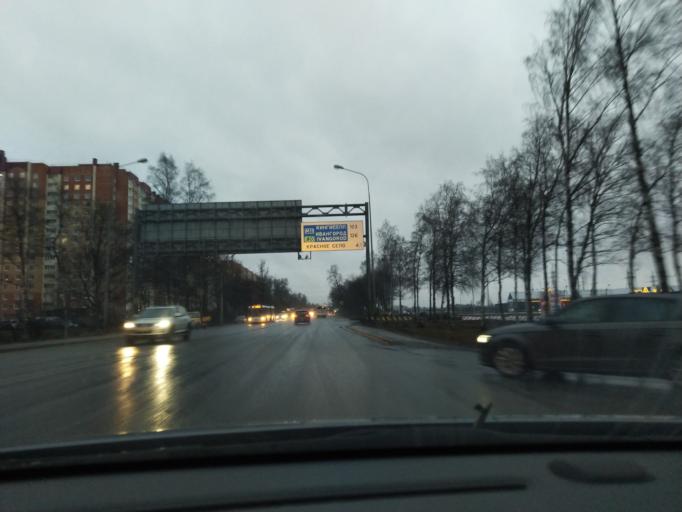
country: RU
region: St.-Petersburg
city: Gorelovo
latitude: 59.7942
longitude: 30.1499
